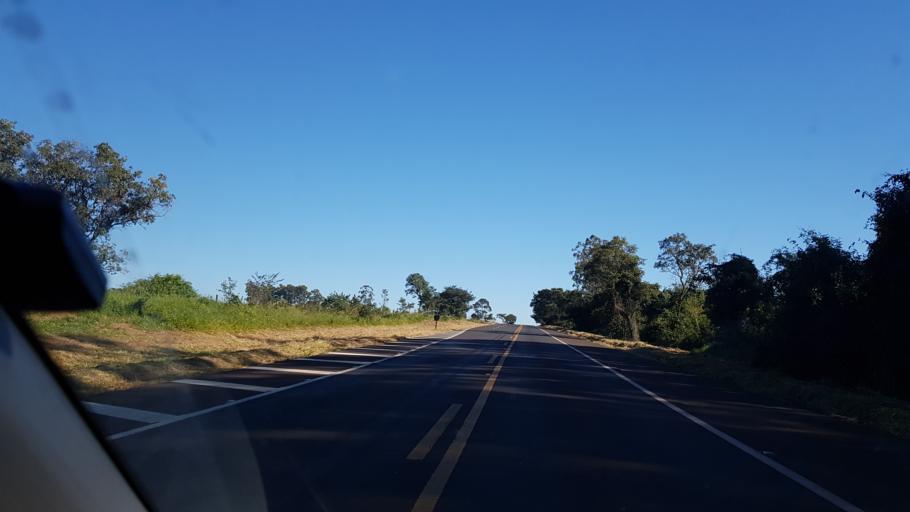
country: BR
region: Sao Paulo
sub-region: Assis
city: Assis
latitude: -22.5791
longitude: -50.5084
